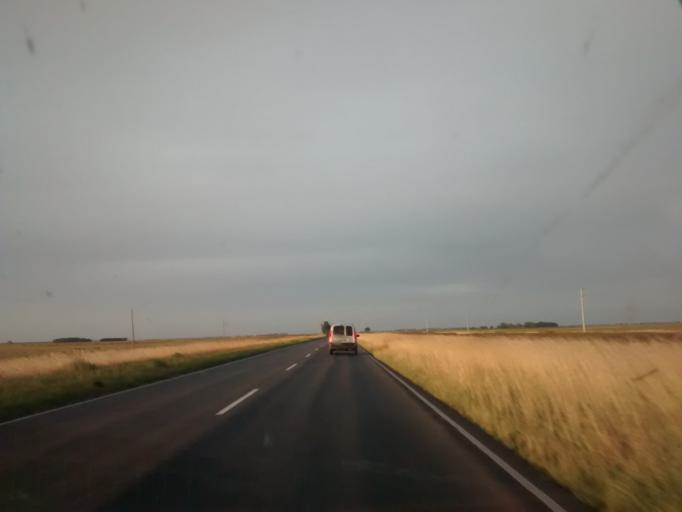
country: AR
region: Buenos Aires
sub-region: Partido de General Belgrano
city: General Belgrano
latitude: -35.9631
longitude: -58.6210
